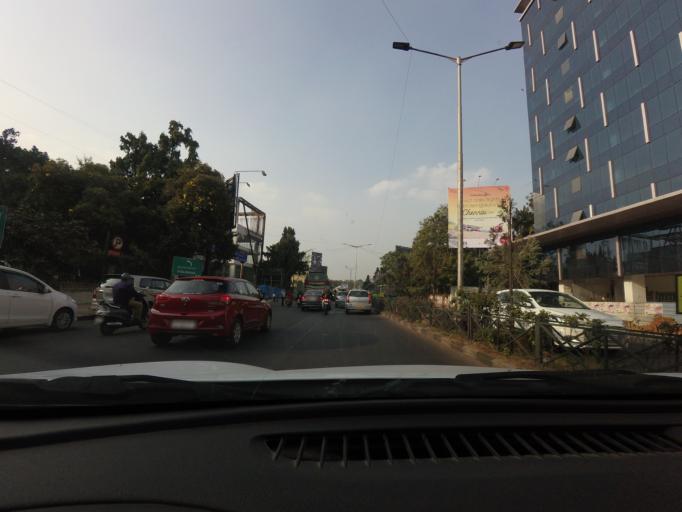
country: IN
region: Karnataka
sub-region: Bangalore Urban
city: Bangalore
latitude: 12.9966
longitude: 77.5846
